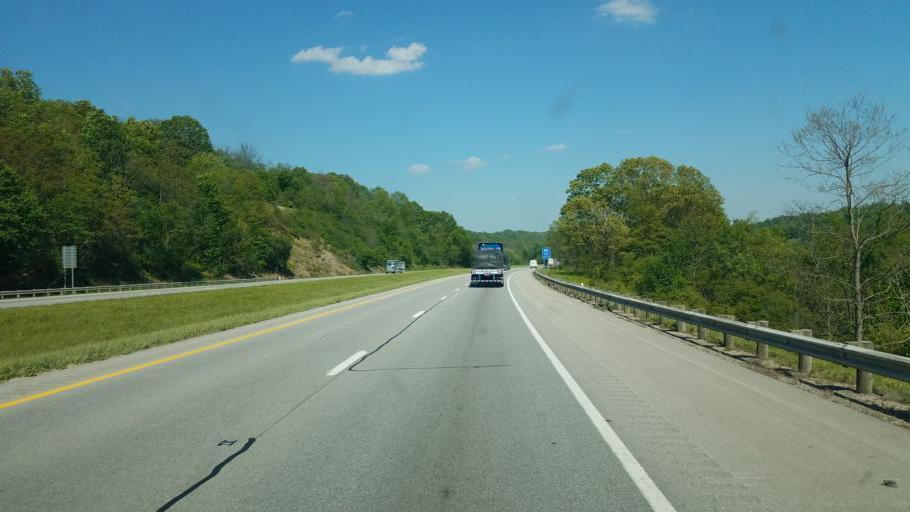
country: US
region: Ohio
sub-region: Guernsey County
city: Byesville
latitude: 40.0043
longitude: -81.5333
